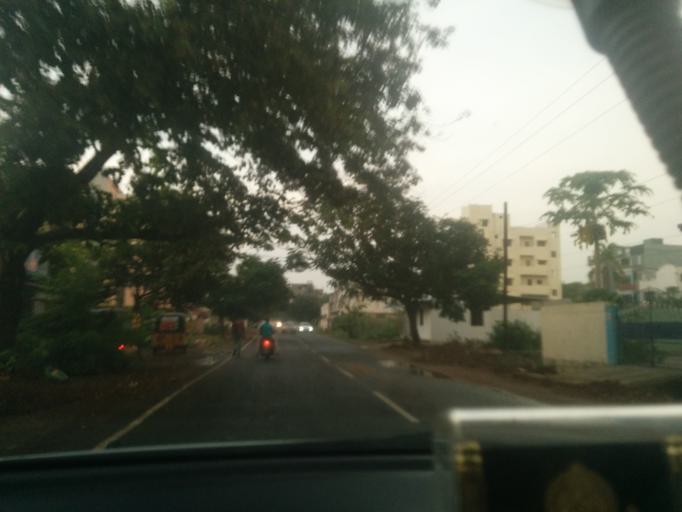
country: IN
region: Andhra Pradesh
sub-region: East Godavari
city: Rajahmundry
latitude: 17.0217
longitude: 81.7935
